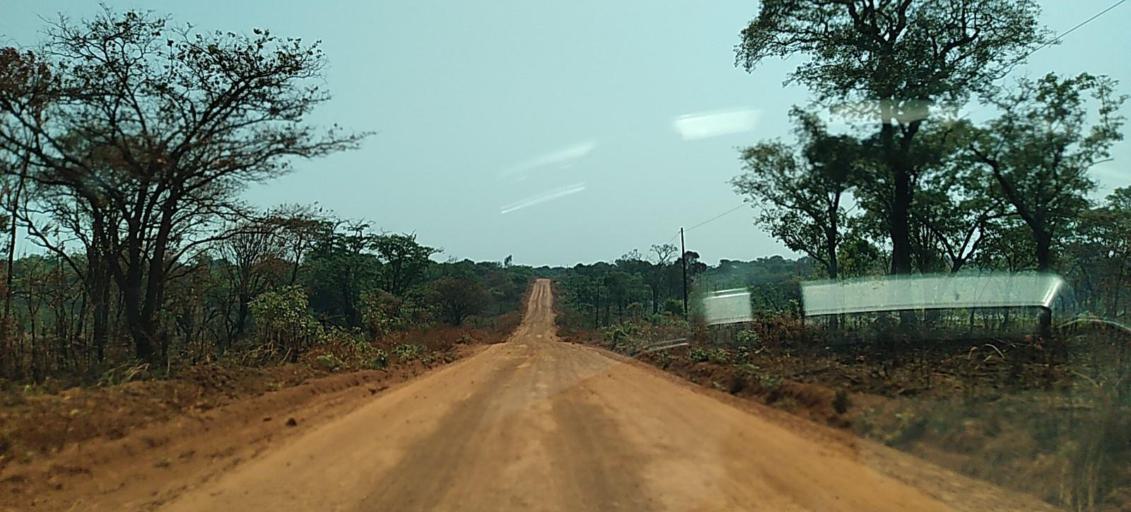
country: ZM
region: North-Western
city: Kansanshi
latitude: -11.9999
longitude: 26.5917
